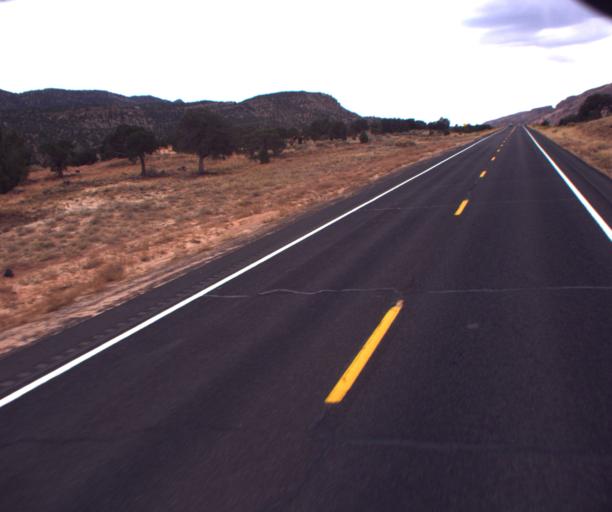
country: US
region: Arizona
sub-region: Navajo County
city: Kayenta
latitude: 36.6798
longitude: -110.3881
